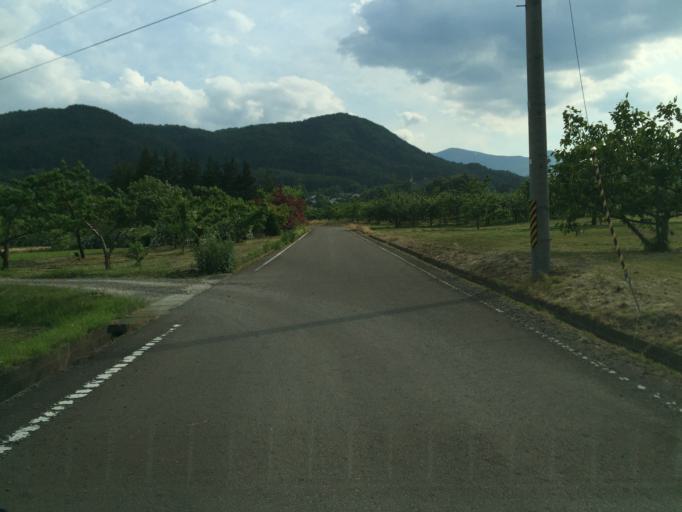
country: JP
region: Fukushima
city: Fukushima-shi
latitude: 37.7087
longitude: 140.3747
